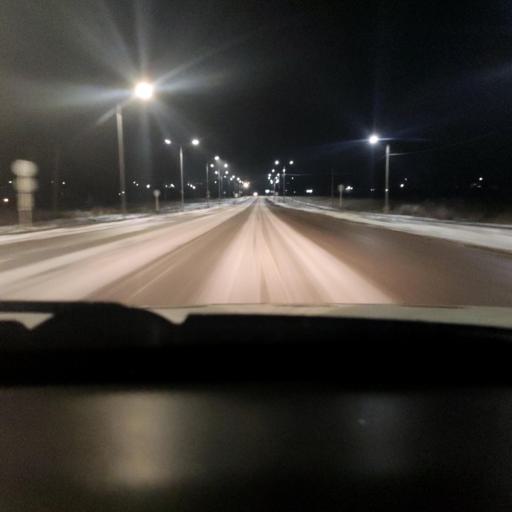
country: RU
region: Perm
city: Kultayevo
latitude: 57.8690
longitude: 55.8708
